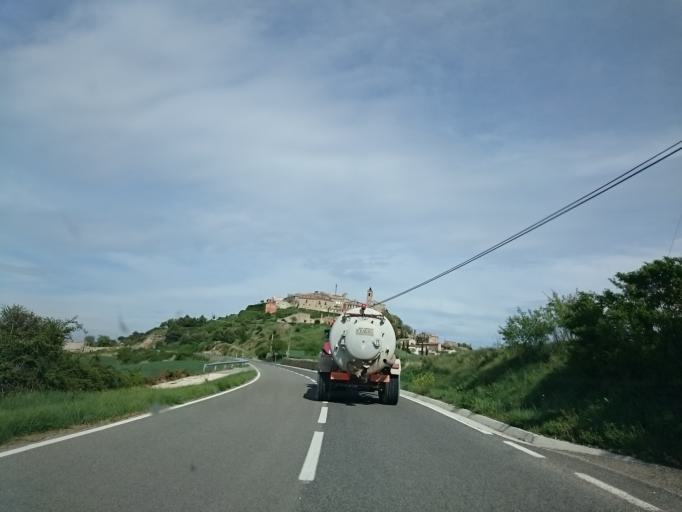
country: ES
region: Catalonia
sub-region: Provincia de Tarragona
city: Santa Coloma de Queralt
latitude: 41.5527
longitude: 1.4133
